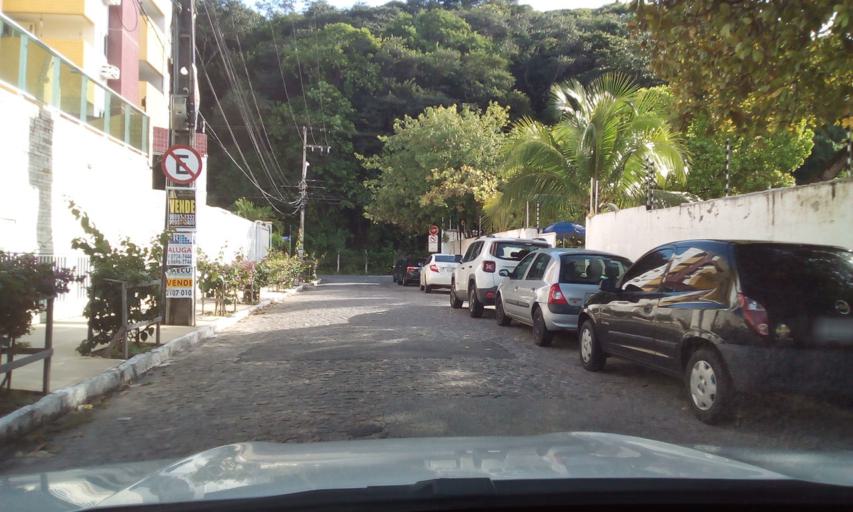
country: BR
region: Paraiba
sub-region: Joao Pessoa
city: Joao Pessoa
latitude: -7.1370
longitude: -34.8199
